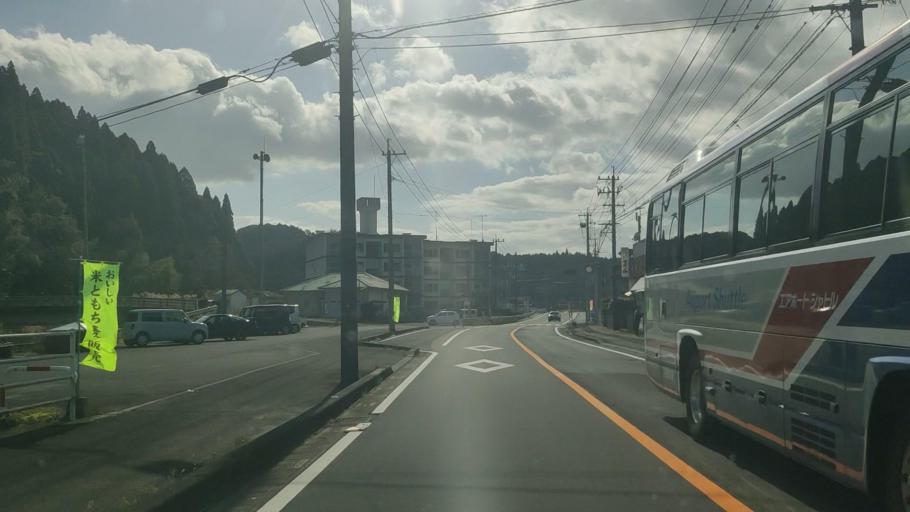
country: JP
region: Kagoshima
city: Okuchi-shinohara
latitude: 31.9433
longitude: 130.7104
